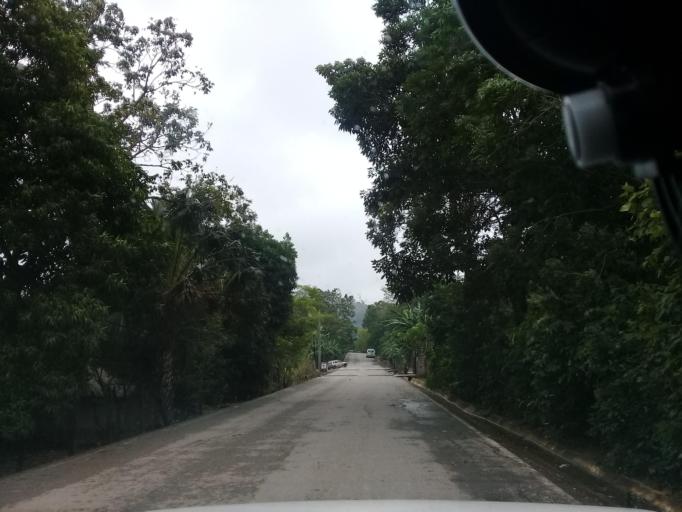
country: MX
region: Veracruz
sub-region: Chalma
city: San Pedro Coyutla
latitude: 21.2229
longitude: -98.4318
